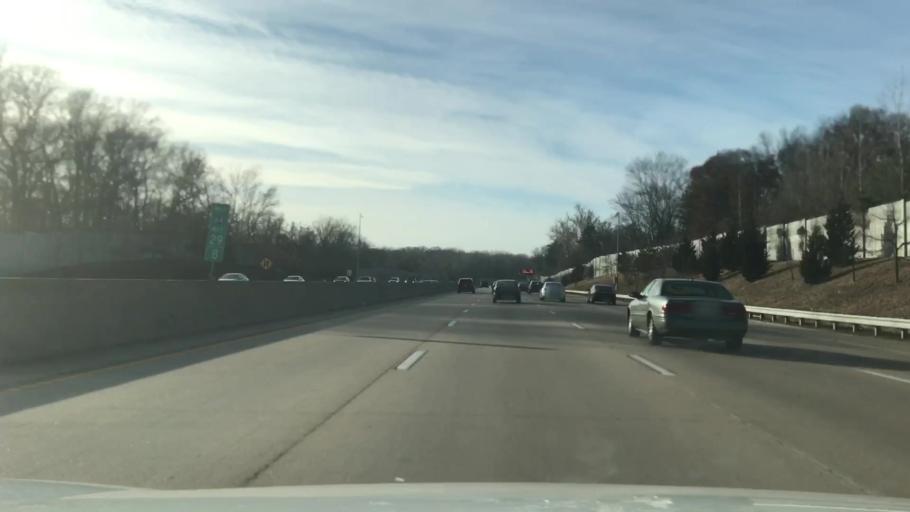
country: US
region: Missouri
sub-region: Saint Louis County
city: Ladue
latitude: 38.6316
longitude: -90.3785
